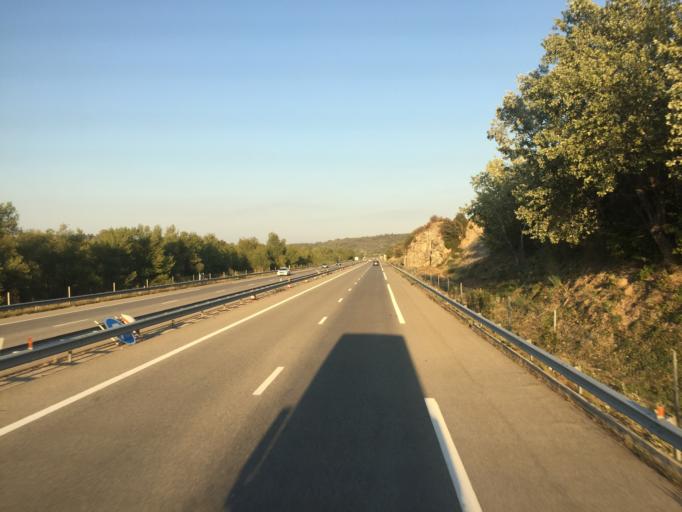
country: FR
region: Provence-Alpes-Cote d'Azur
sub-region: Departement du Vaucluse
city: Beaumont-de-Pertuis
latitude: 43.6901
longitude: 5.6905
